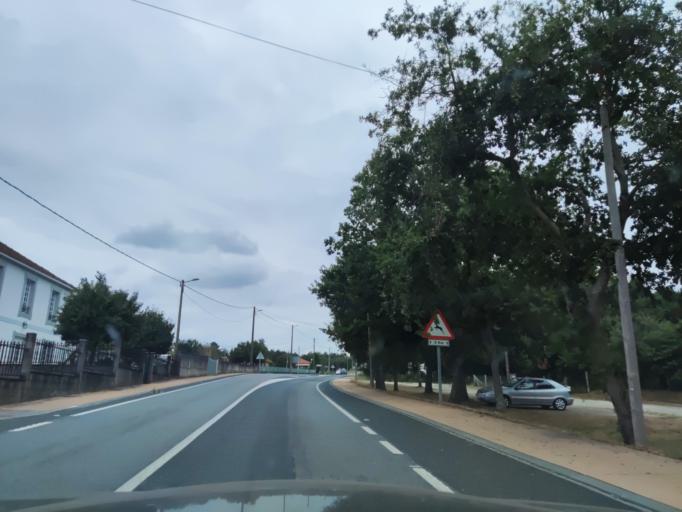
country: ES
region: Galicia
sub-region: Provincia da Coruna
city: Teo
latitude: 42.7662
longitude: -8.5487
